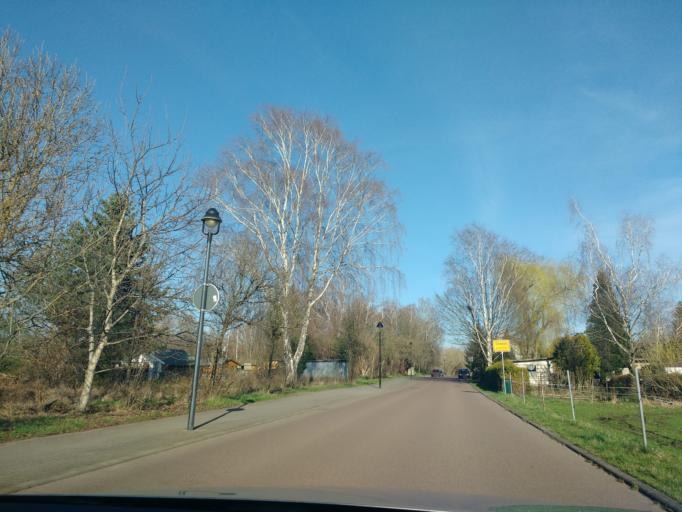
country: DE
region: Saxony-Anhalt
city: Gutenberg
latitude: 51.5307
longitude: 11.9651
